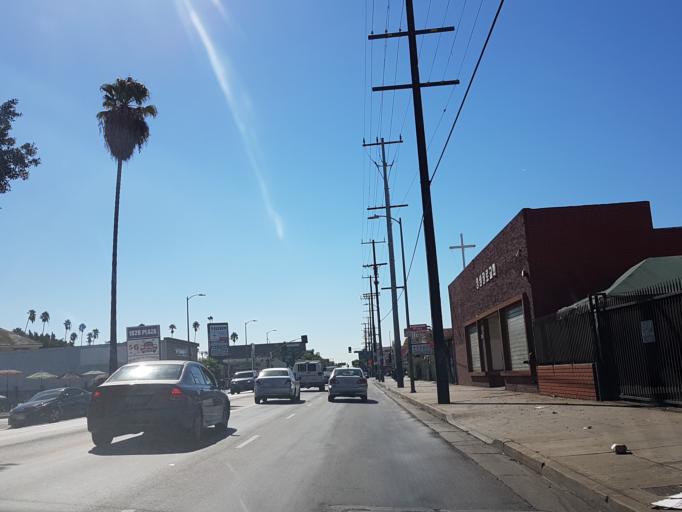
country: US
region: California
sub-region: Los Angeles County
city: Hollywood
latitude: 34.0412
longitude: -118.3091
